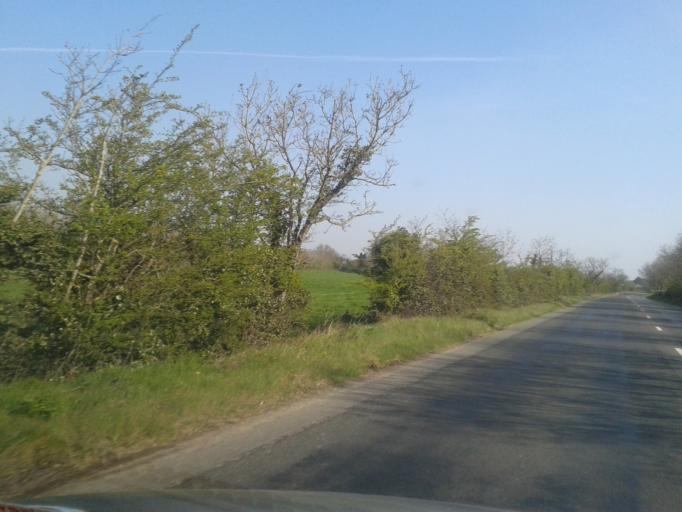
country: IE
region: Leinster
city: Balrothery
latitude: 53.5794
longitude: -6.1996
